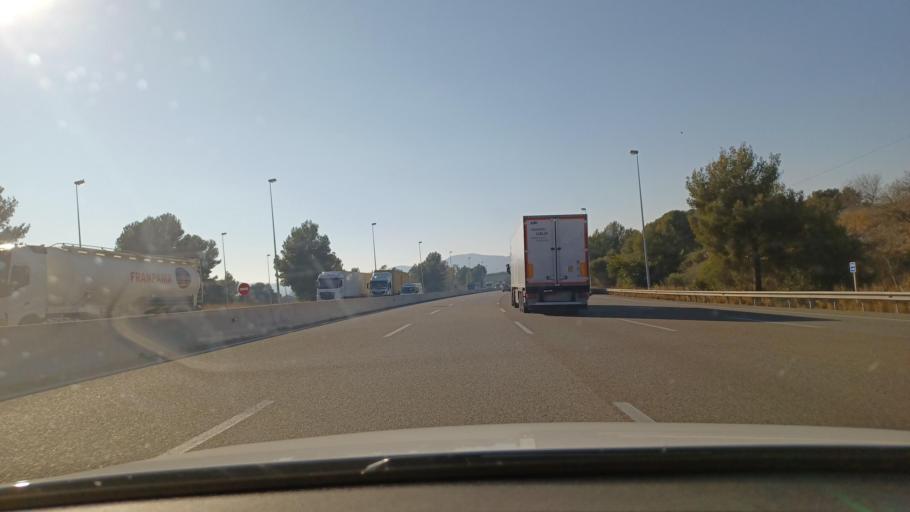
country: ES
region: Catalonia
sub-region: Provincia de Tarragona
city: Santa Oliva
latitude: 41.2708
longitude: 1.5511
